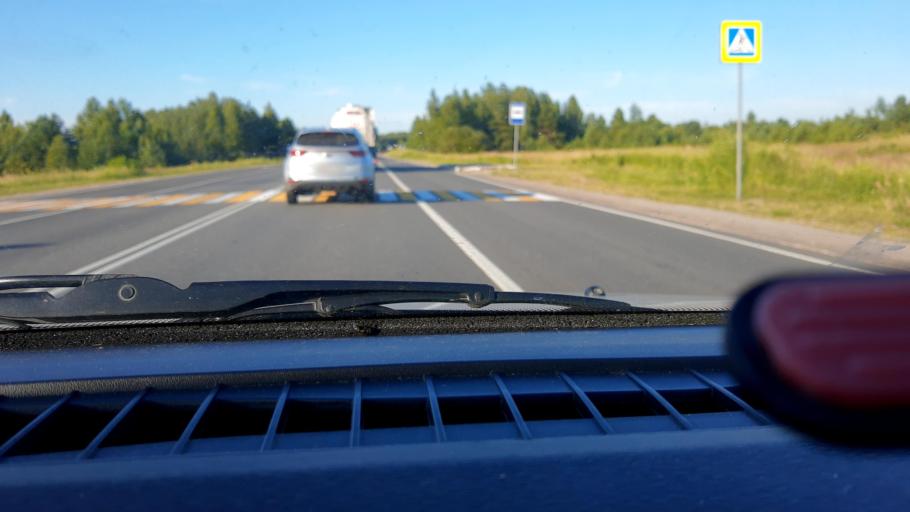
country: RU
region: Nizjnij Novgorod
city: Semenov
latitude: 56.7296
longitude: 44.2982
